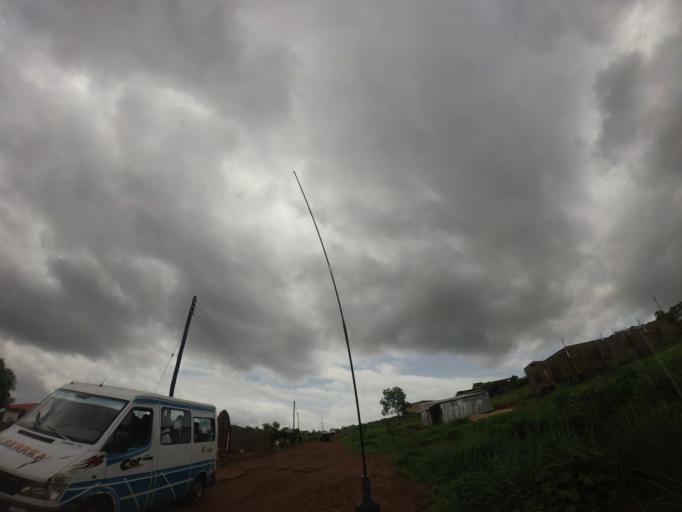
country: SL
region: Western Area
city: Hastings
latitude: 8.3848
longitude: -13.1263
